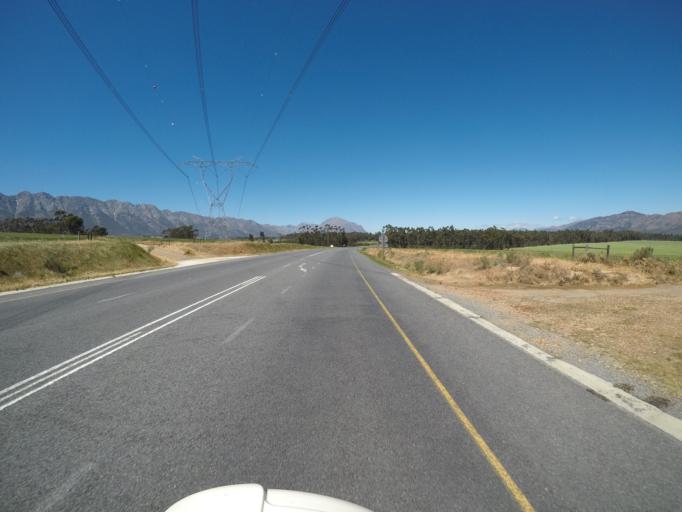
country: ZA
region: Western Cape
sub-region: Cape Winelands District Municipality
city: Ceres
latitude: -33.3292
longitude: 19.1558
